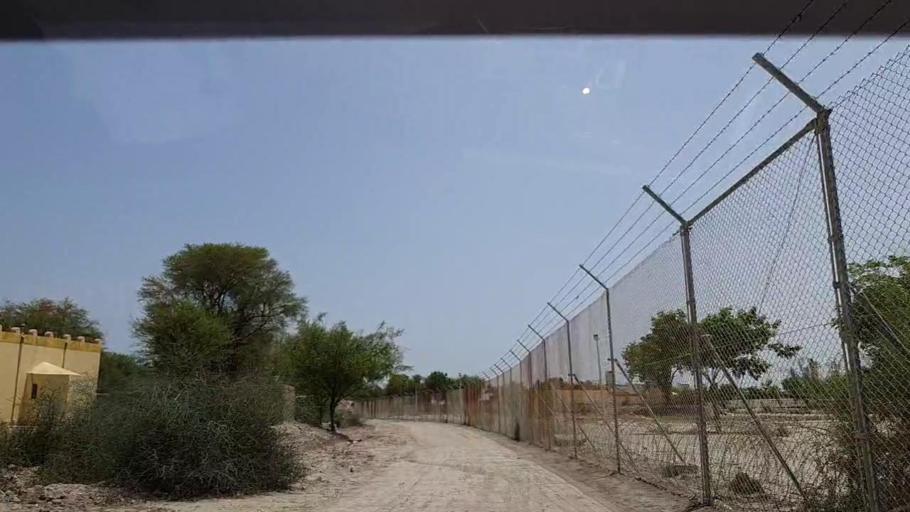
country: PK
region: Sindh
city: Johi
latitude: 26.7103
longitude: 67.6677
